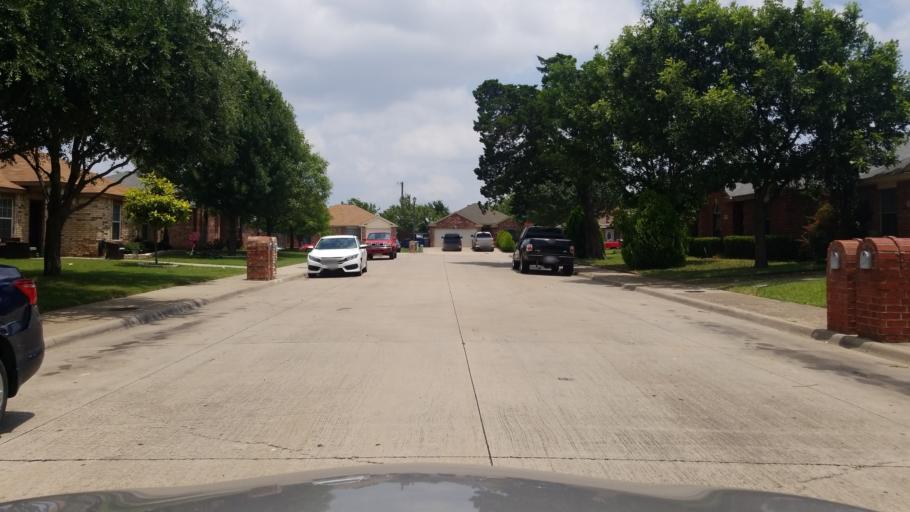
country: US
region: Texas
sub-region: Dallas County
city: Duncanville
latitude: 32.6863
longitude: -96.9138
